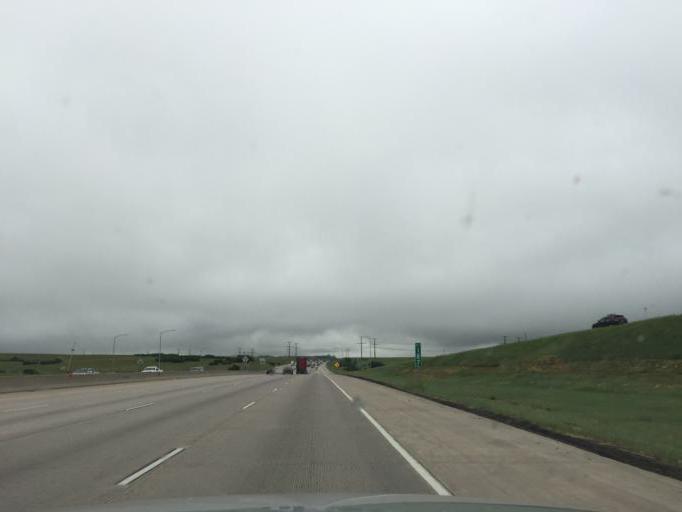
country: US
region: Colorado
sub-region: Douglas County
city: Castle Pines
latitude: 39.4500
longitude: -104.8755
